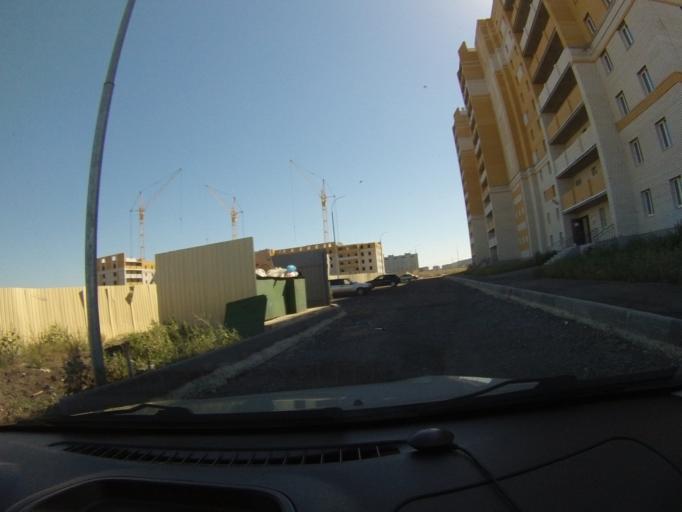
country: RU
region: Tambov
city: Tambov
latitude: 52.7797
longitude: 41.4063
